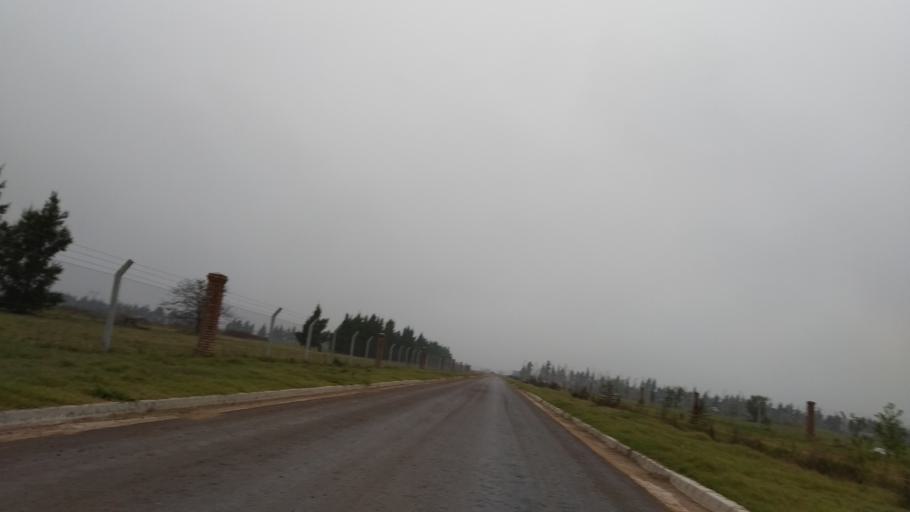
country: AR
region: Santa Fe
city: Funes
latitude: -32.9437
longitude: -60.7688
